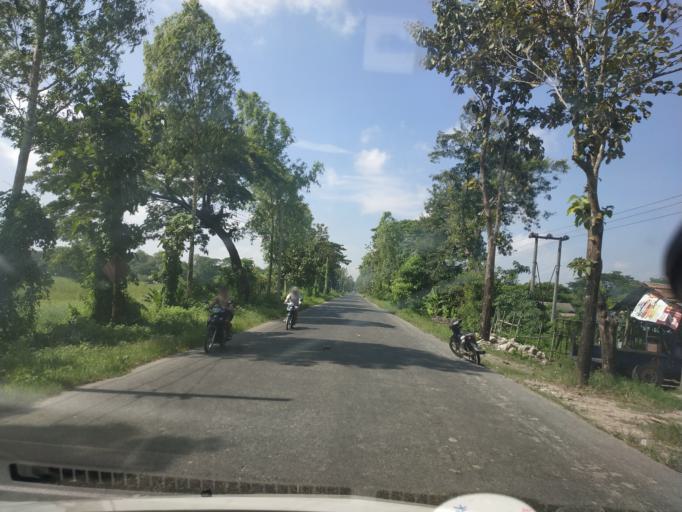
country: MM
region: Ayeyarwady
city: Nyaungdon
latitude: 17.0445
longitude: 95.5443
